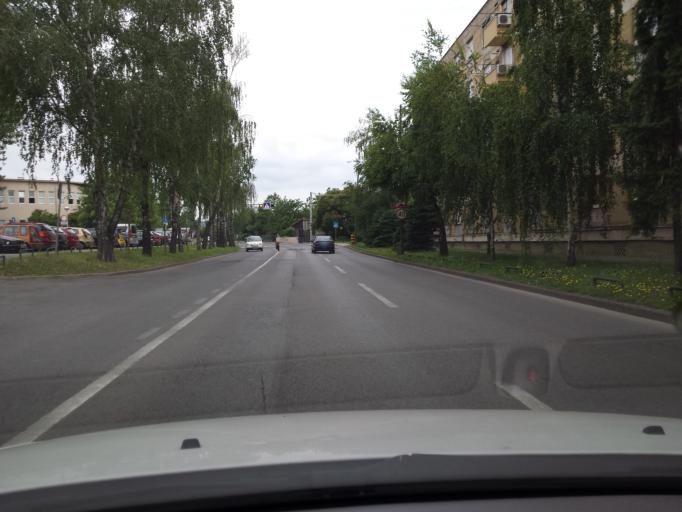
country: HR
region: Grad Zagreb
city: Zagreb - Centar
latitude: 45.8038
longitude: 15.9477
